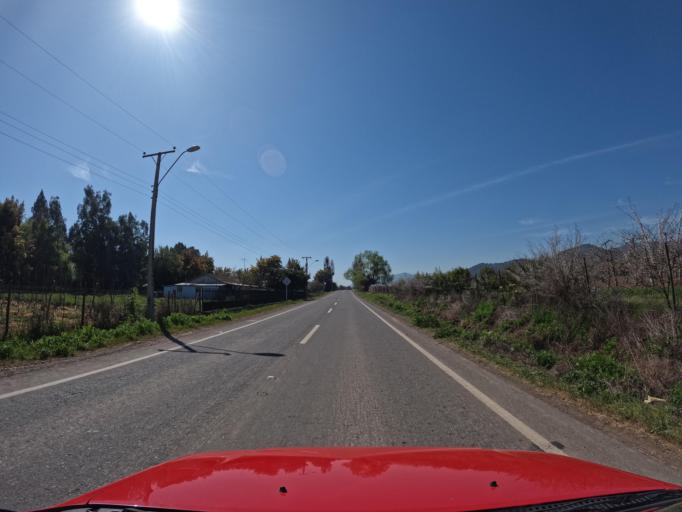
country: CL
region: Maule
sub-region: Provincia de Curico
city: Molina
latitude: -35.0539
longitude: -71.4812
